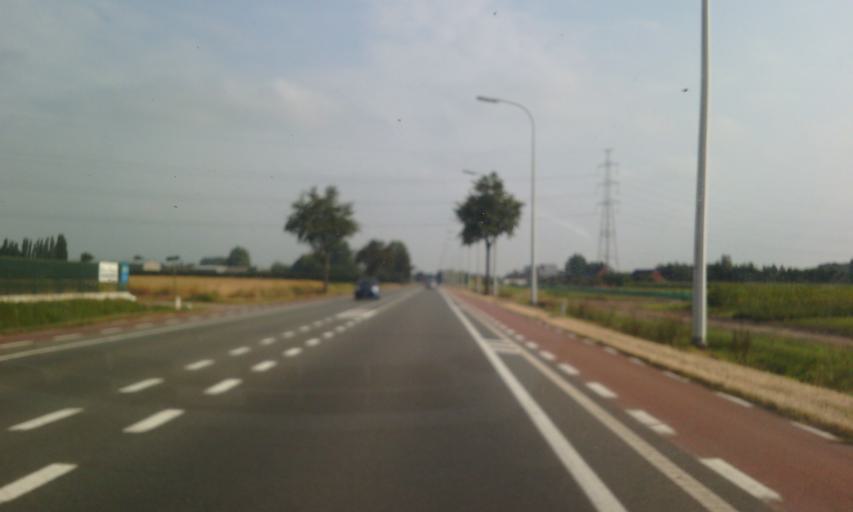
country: BE
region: Flanders
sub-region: Provincie Oost-Vlaanderen
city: Lovendegem
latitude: 51.1220
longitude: 3.6096
